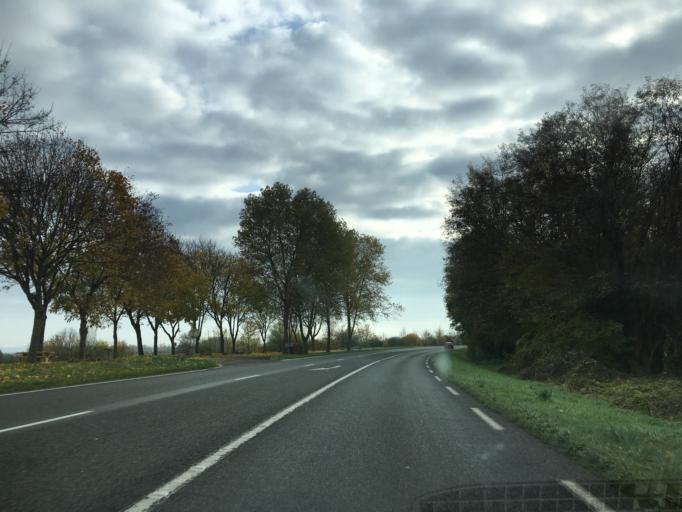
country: FR
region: Bourgogne
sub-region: Departement de l'Yonne
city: Pont-sur-Yonne
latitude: 48.2669
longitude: 3.2351
